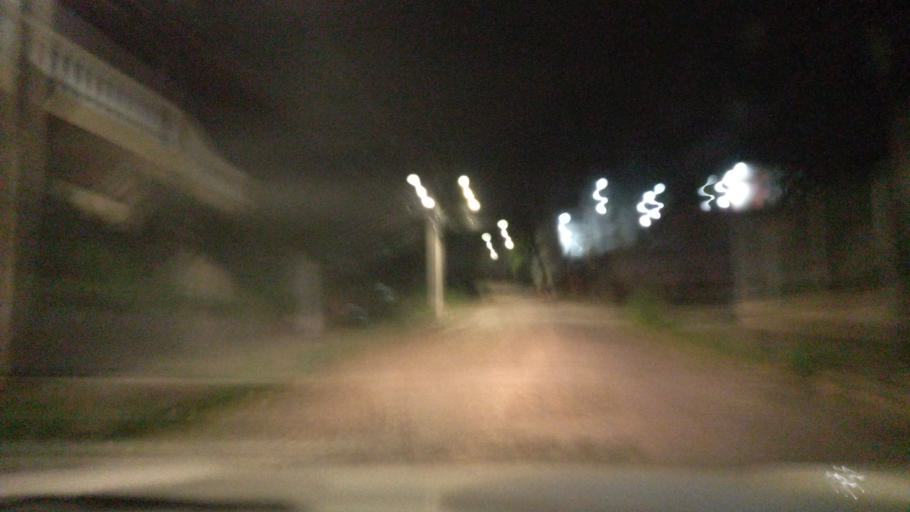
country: BR
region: Minas Gerais
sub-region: Belo Horizonte
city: Belo Horizonte
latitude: -19.8797
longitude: -43.9440
